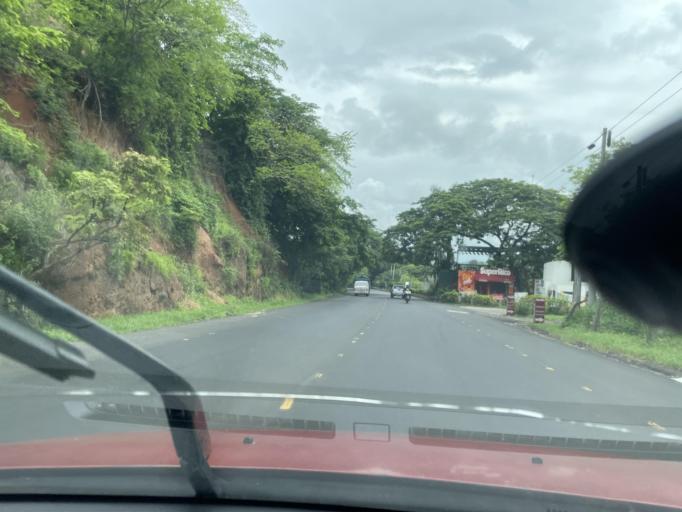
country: SV
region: San Miguel
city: Chirilagua
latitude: 13.3380
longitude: -88.1464
